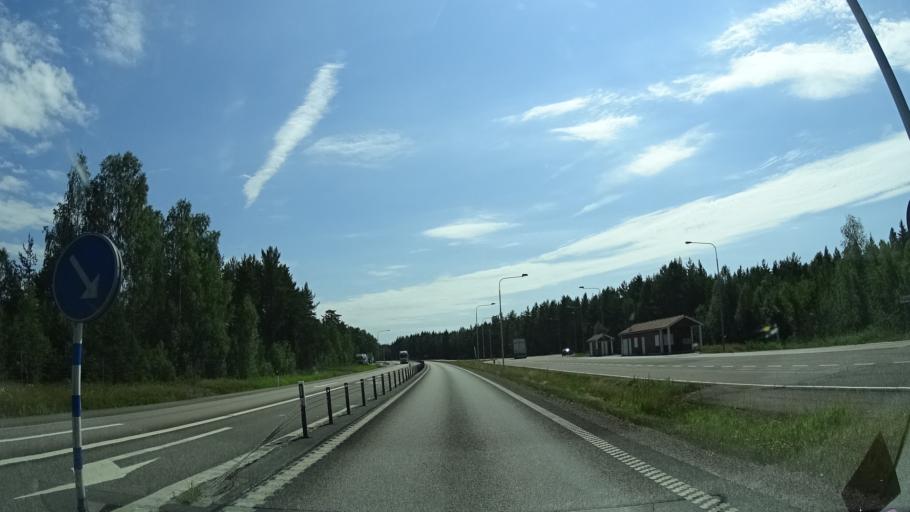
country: SE
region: Vaermland
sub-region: Kristinehamns Kommun
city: Kristinehamn
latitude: 59.3635
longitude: 14.0251
